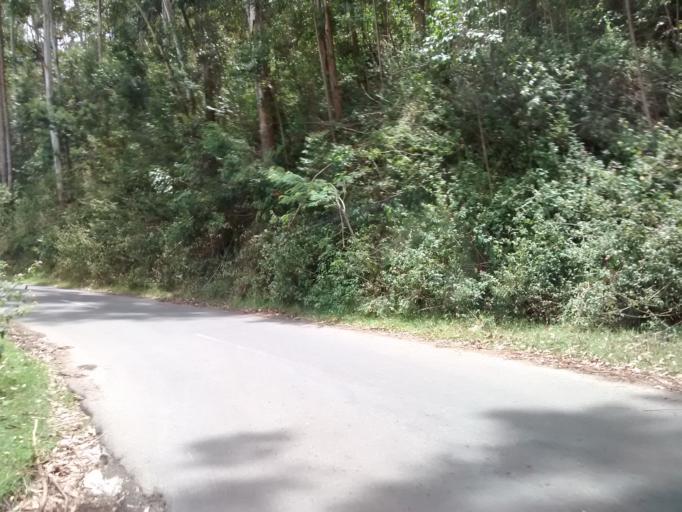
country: IN
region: Kerala
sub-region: Idukki
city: Munnar
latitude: 10.1385
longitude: 77.1927
